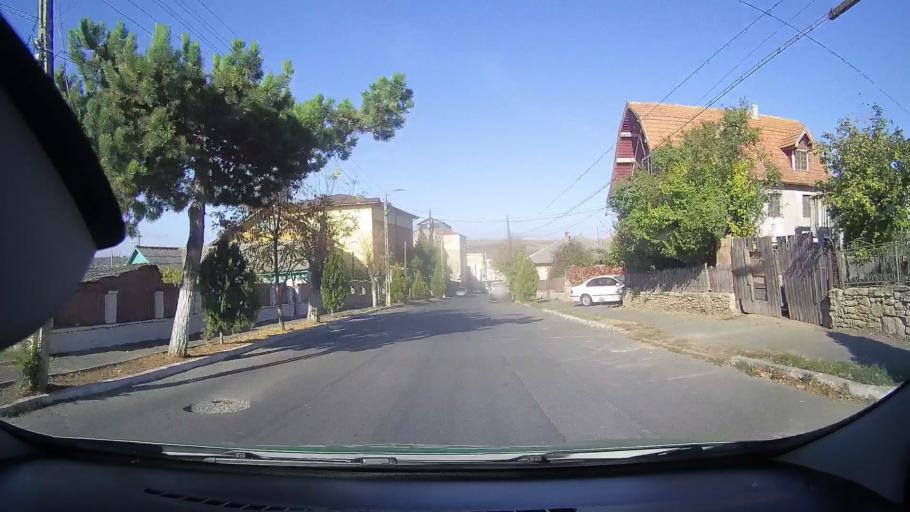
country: RO
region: Tulcea
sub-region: Oras Babadag
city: Babadag
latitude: 44.8923
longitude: 28.7263
